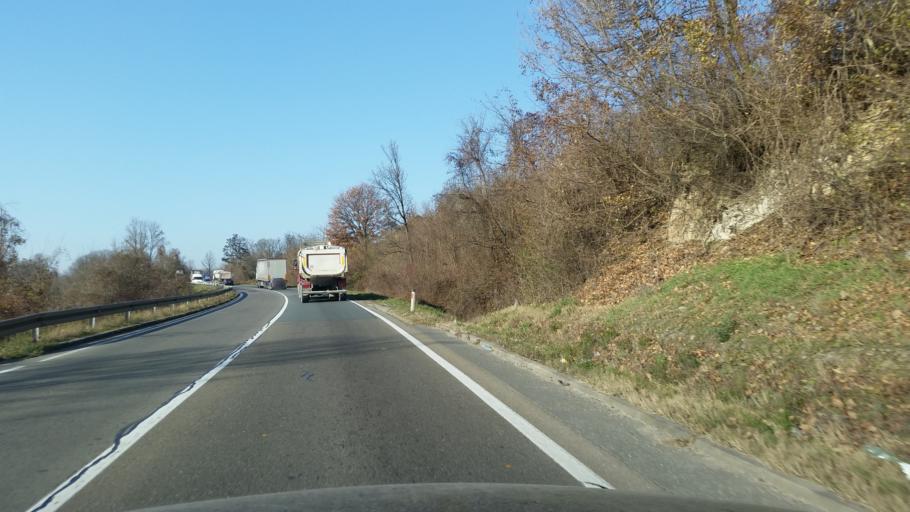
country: RS
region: Central Serbia
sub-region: Kolubarski Okrug
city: Lajkovac
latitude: 44.3470
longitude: 20.1966
